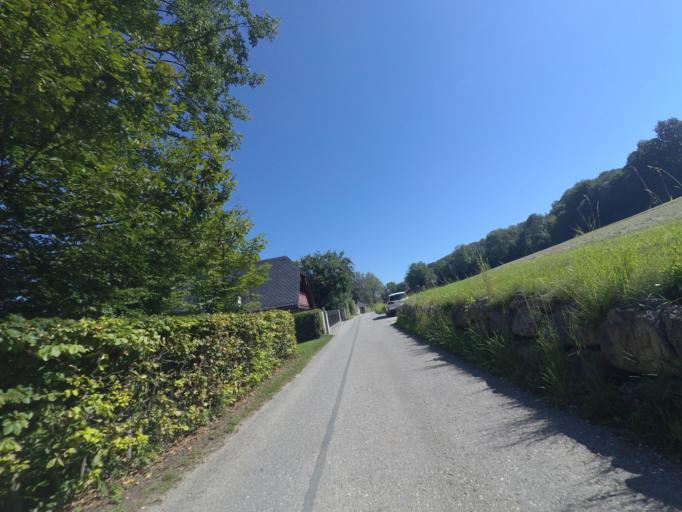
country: AT
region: Salzburg
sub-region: Politischer Bezirk Salzburg-Umgebung
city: Mattsee
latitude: 47.9718
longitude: 13.1153
